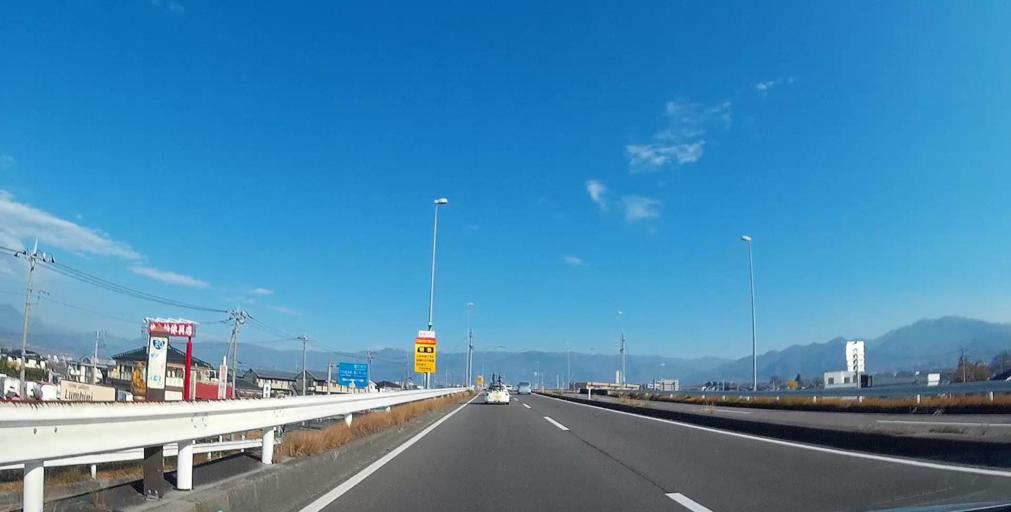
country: JP
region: Yamanashi
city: Isawa
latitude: 35.6434
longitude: 138.6486
